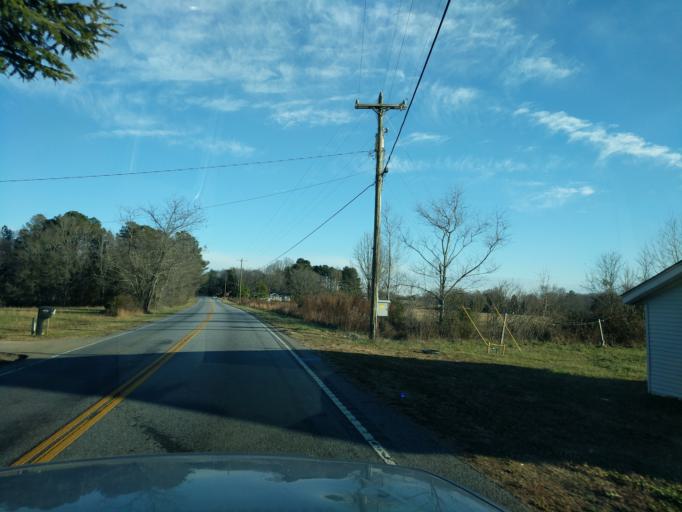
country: US
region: South Carolina
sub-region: Anderson County
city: Williamston
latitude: 34.6602
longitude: -82.5048
